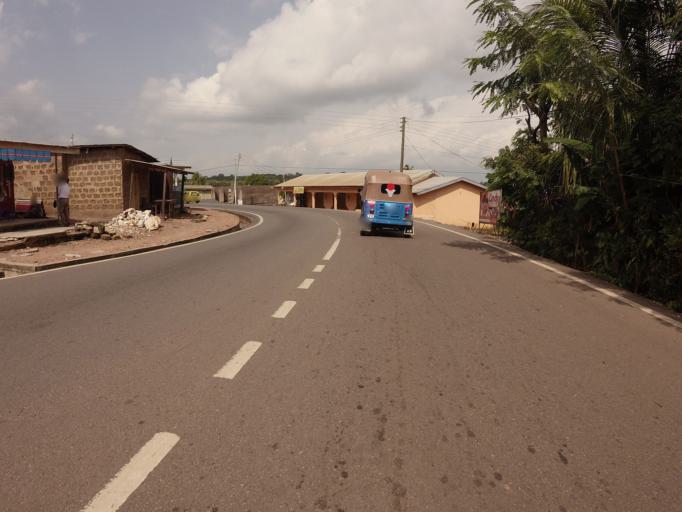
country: GH
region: Volta
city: Ho
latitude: 6.6202
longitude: 0.4768
